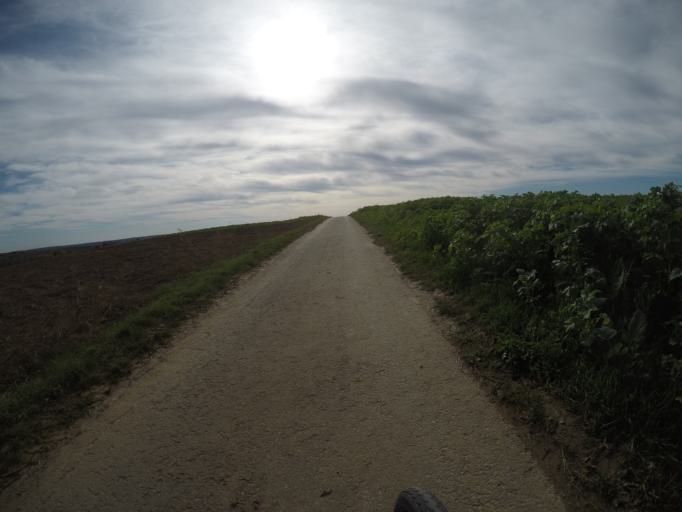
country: DE
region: Baden-Wuerttemberg
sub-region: Regierungsbezirk Stuttgart
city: Deckenpfronn
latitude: 48.6395
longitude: 8.8401
